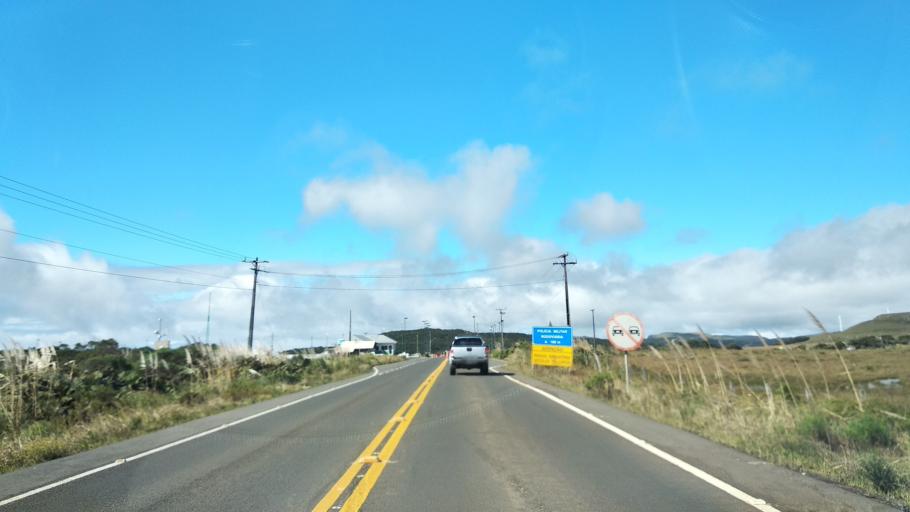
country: BR
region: Santa Catarina
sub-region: Lauro Muller
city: Lauro Muller
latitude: -28.3920
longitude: -49.5508
